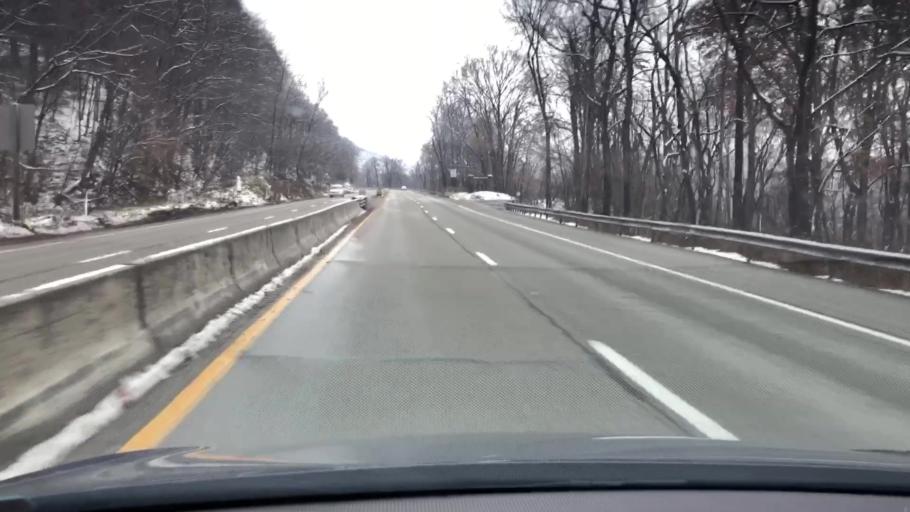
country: US
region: Pennsylvania
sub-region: Fayette County
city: Hopwood
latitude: 39.8637
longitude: -79.6786
